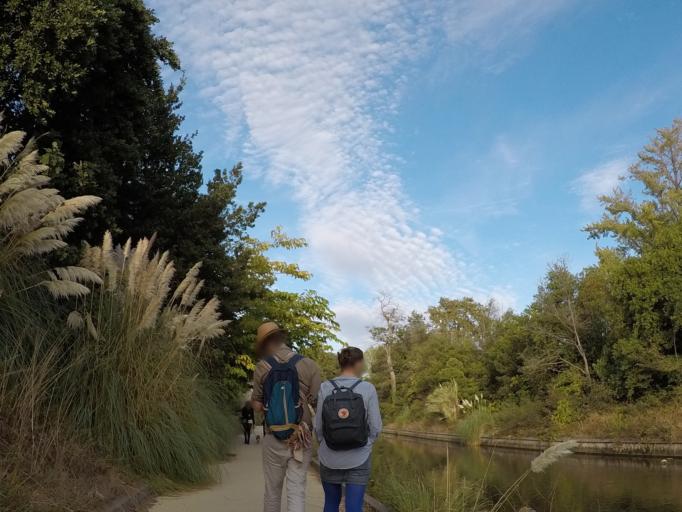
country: FR
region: Provence-Alpes-Cote d'Azur
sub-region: Departement des Bouches-du-Rhone
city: Marseille 08
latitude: 43.2625
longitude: 5.3818
